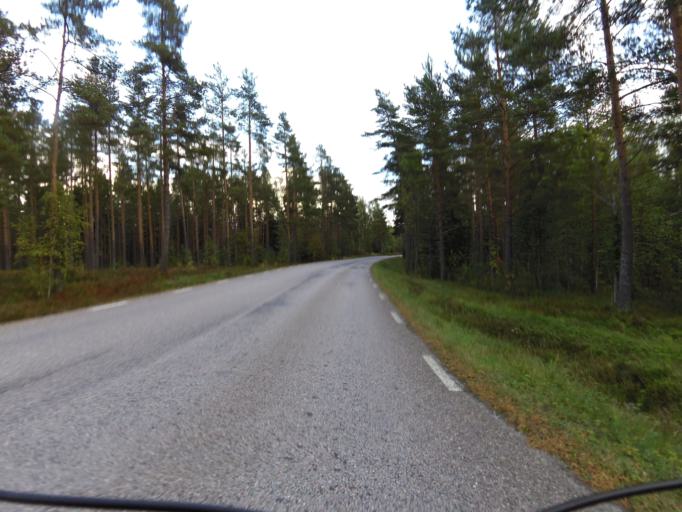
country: SE
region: Gaevleborg
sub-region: Gavle Kommun
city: Valbo
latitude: 60.6669
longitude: 16.9438
